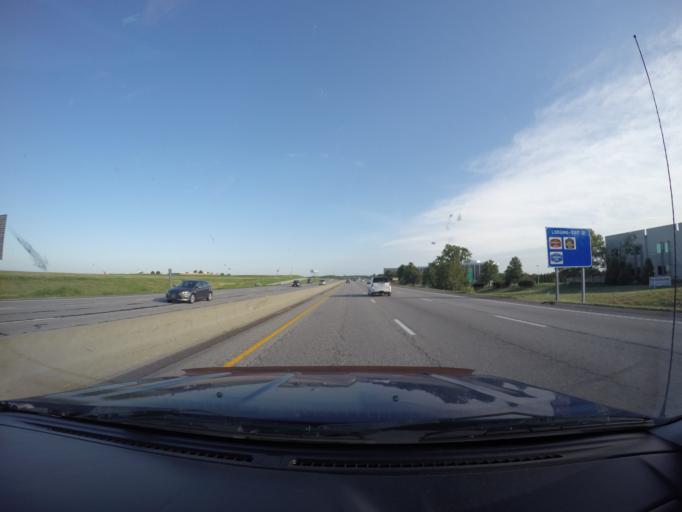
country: US
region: Missouri
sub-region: Platte County
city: Weatherby Lake
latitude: 39.2877
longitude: -94.6798
